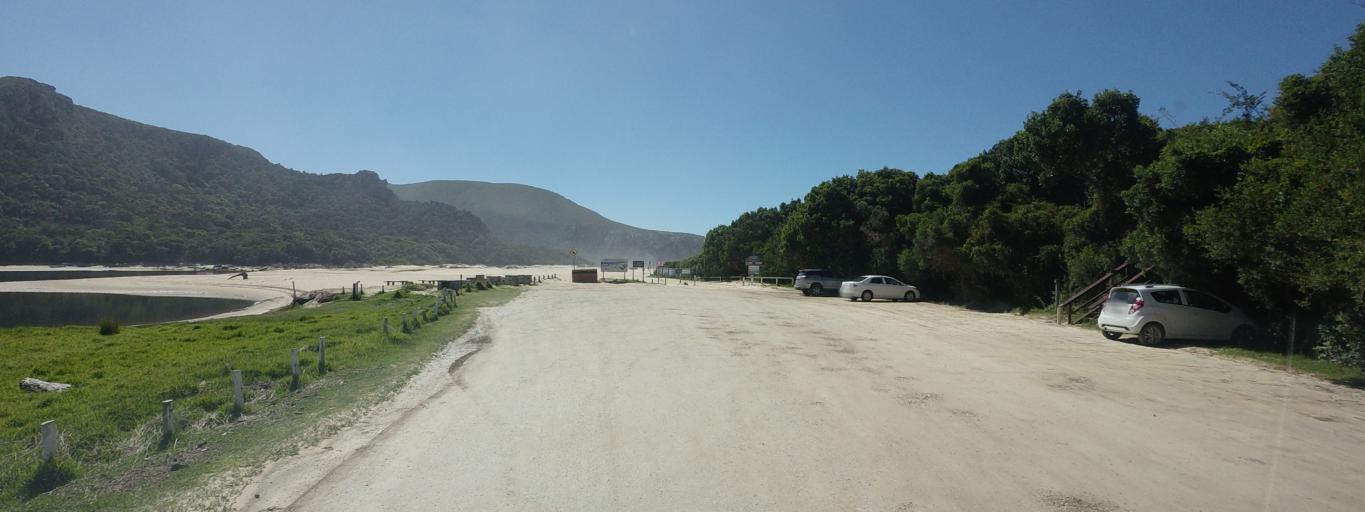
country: ZA
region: Western Cape
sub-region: Eden District Municipality
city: Plettenberg Bay
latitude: -33.9806
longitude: 23.5661
